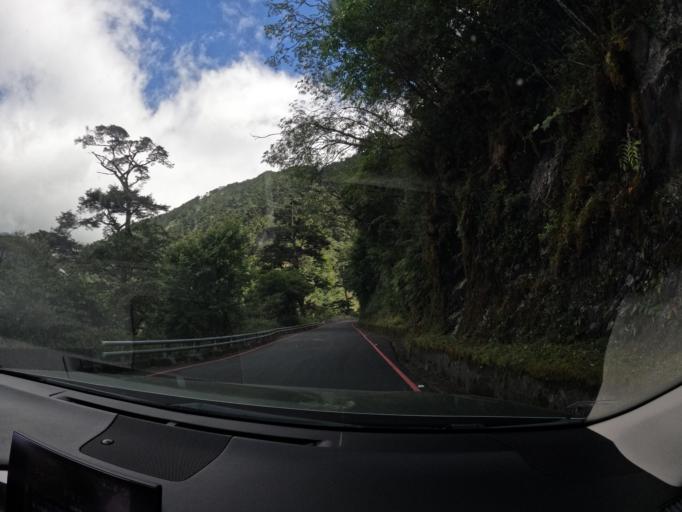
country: TW
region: Taiwan
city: Yujing
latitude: 23.2595
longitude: 120.9440
